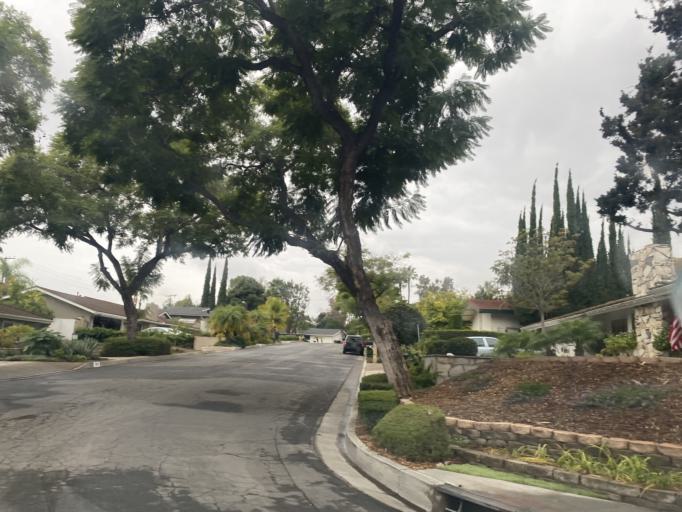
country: US
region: California
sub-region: Orange County
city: Fullerton
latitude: 33.8818
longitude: -117.9158
